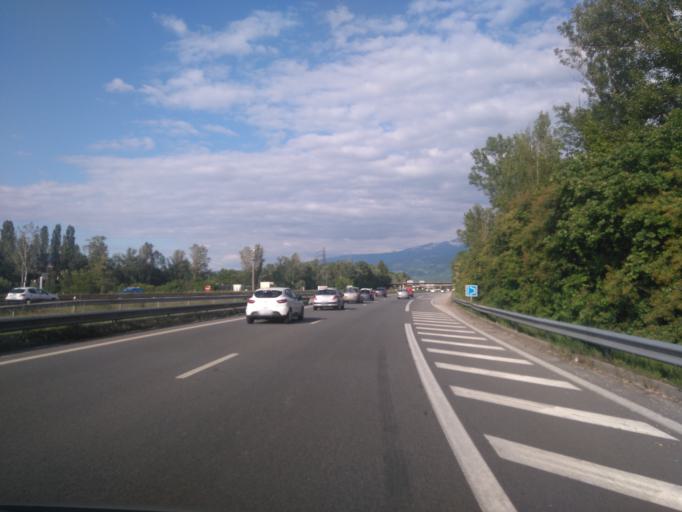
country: FR
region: Rhone-Alpes
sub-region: Departement de l'Isere
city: Corenc
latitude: 45.2042
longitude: 5.7839
